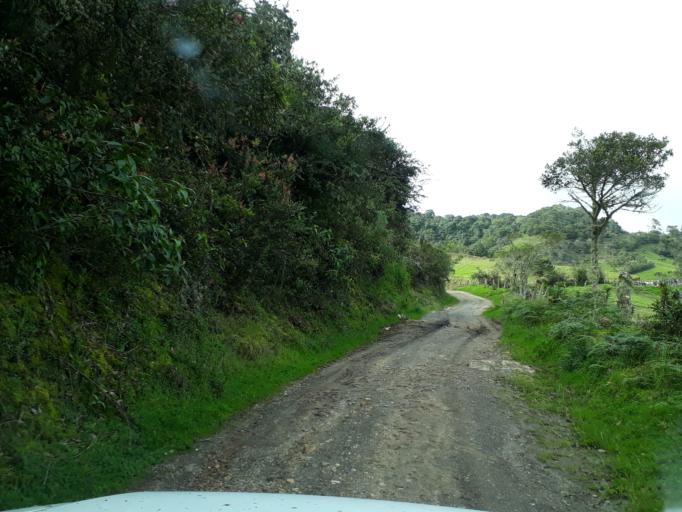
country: CO
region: Cundinamarca
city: Junin
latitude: 4.8266
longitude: -73.7678
